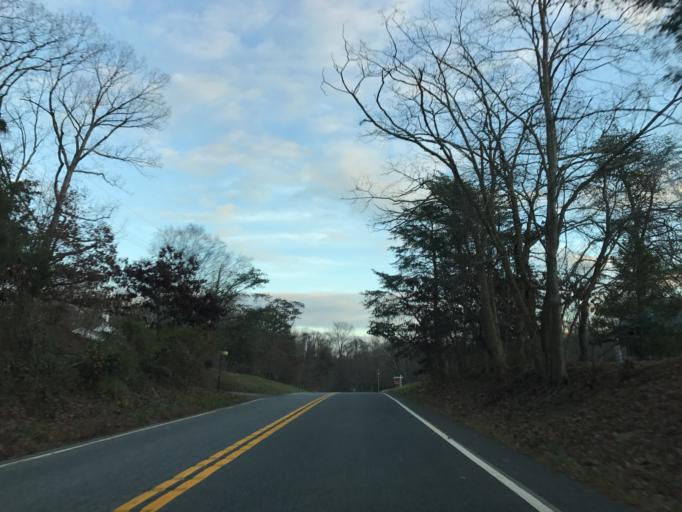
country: US
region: Pennsylvania
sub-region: York County
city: Susquehanna Trails
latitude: 39.6890
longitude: -76.2334
